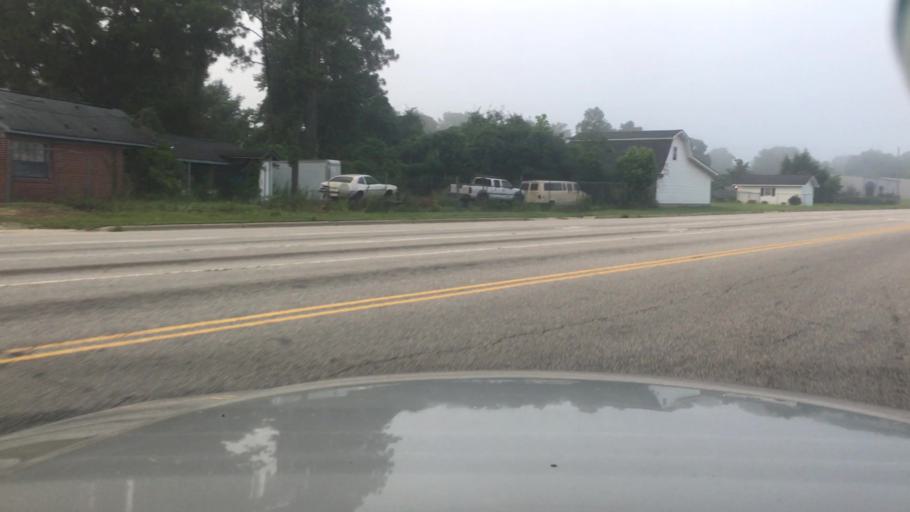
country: US
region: North Carolina
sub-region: Cumberland County
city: Fayetteville
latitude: 35.0180
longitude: -78.9186
